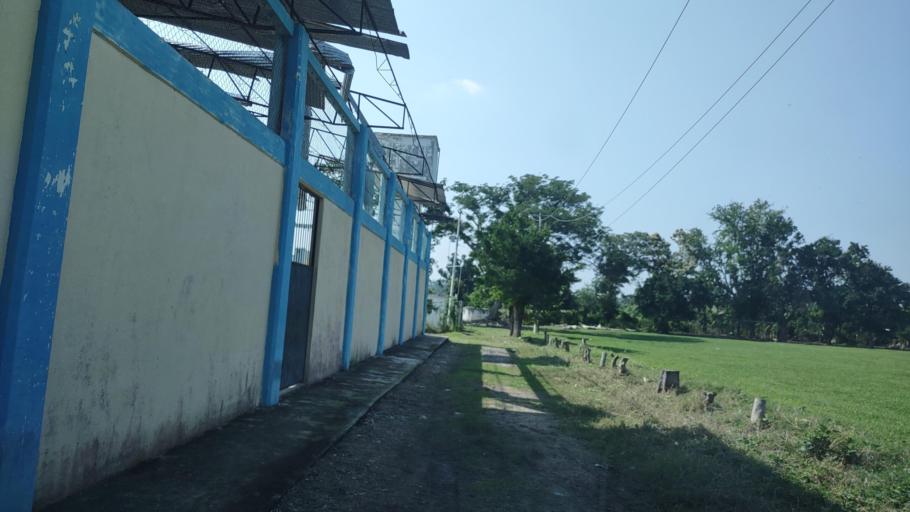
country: MX
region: Puebla
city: Espinal
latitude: 20.2511
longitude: -97.3358
